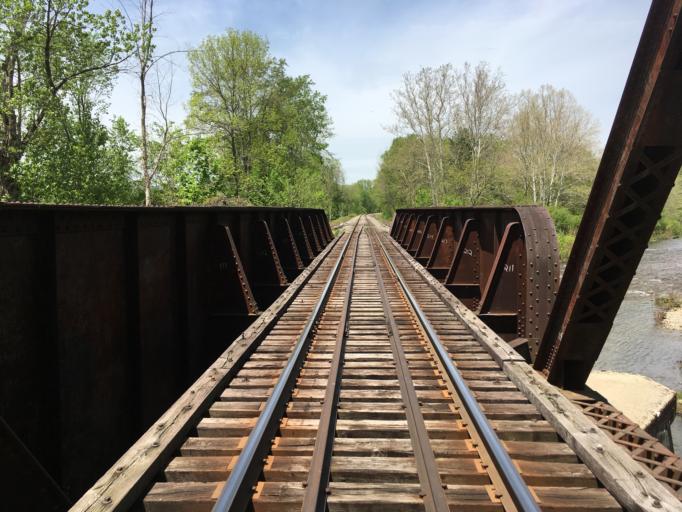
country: US
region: Vermont
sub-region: Windsor County
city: Chester
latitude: 43.2526
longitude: -72.5727
